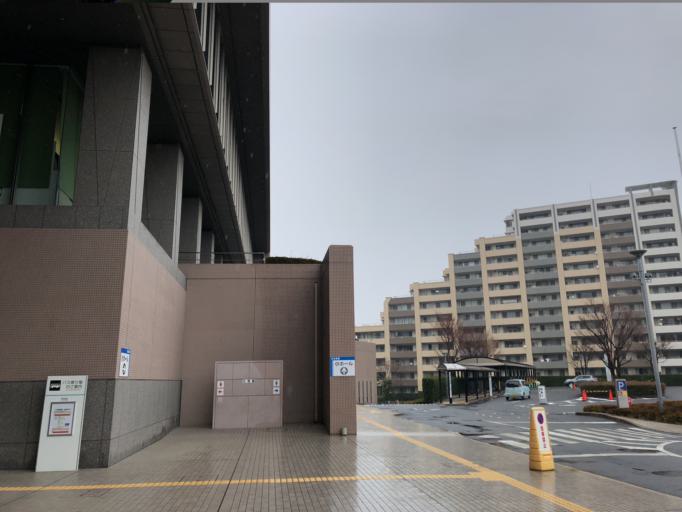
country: JP
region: Mie
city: Tsu-shi
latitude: 34.7441
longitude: 136.5017
